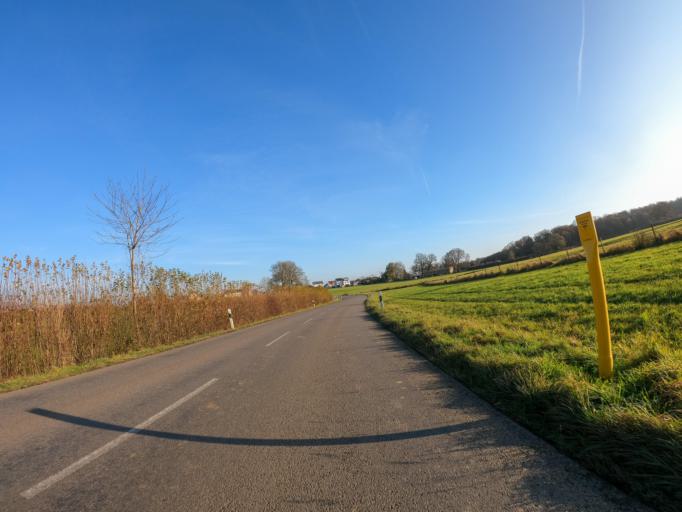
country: LU
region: Luxembourg
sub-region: Canton de Capellen
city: Garnich
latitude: 49.5993
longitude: 5.9385
